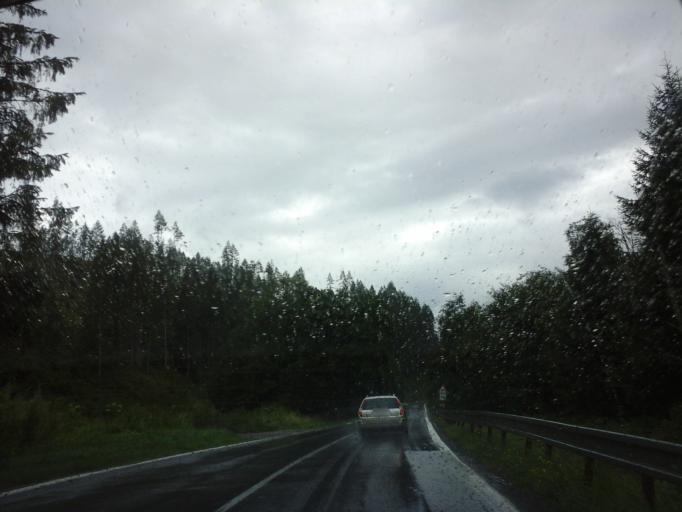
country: SK
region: Presovsky
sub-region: Okres Poprad
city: Poprad
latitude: 48.9627
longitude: 20.2920
